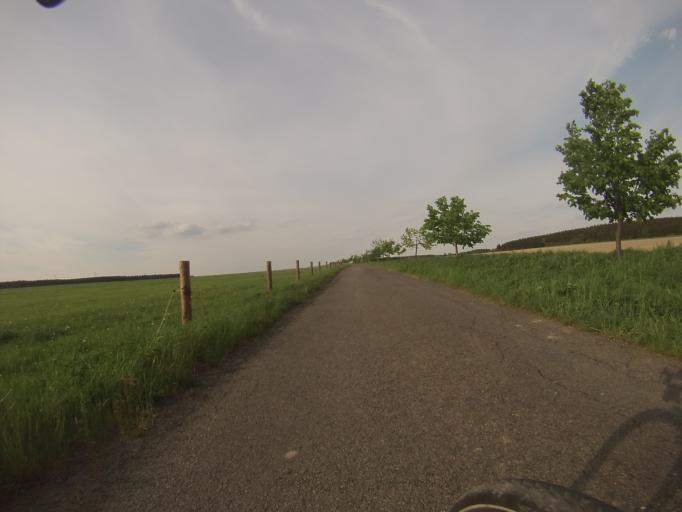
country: CZ
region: Olomoucky
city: Protivanov
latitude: 49.4478
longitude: 16.8628
